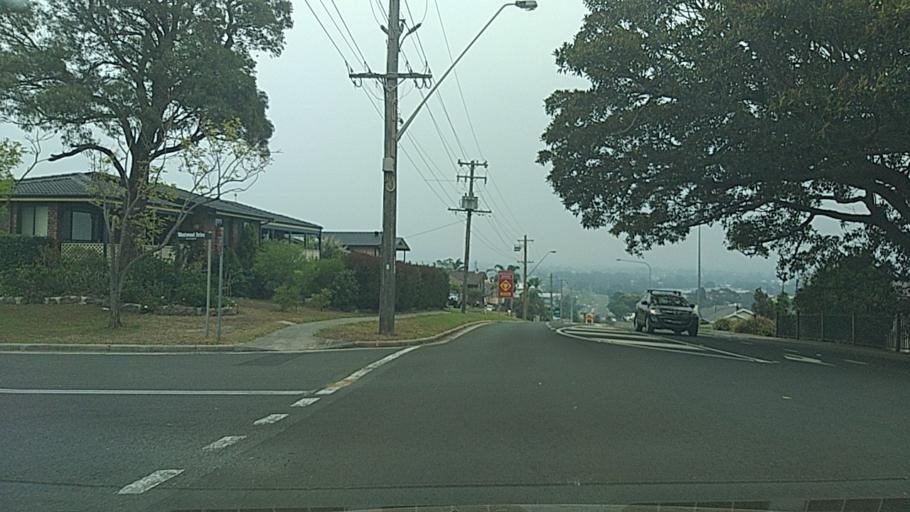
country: AU
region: New South Wales
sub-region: Shellharbour
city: Croom
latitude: -34.5711
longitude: 150.8263
